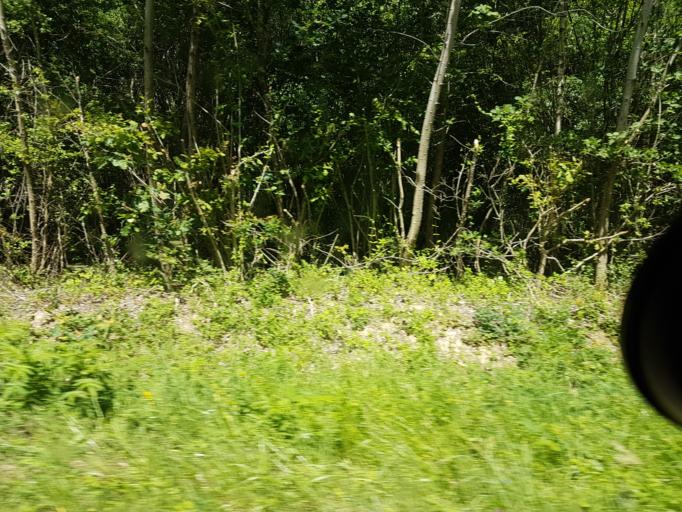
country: FR
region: Bourgogne
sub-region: Departement de Saone-et-Loire
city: Curgy
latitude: 47.0550
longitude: 4.3334
